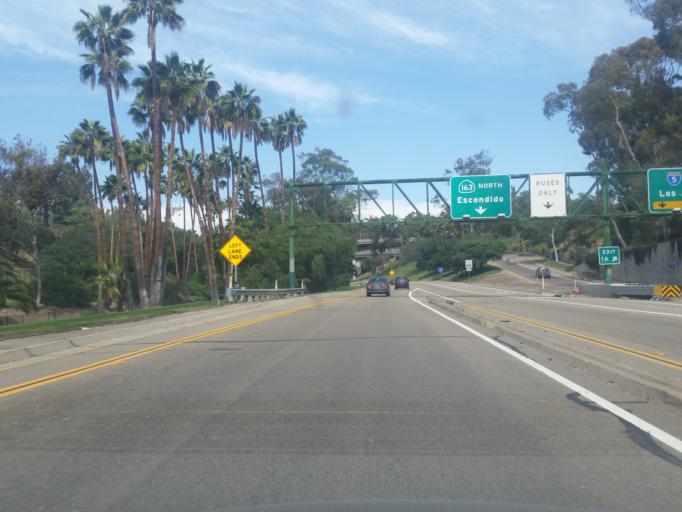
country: US
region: California
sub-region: San Diego County
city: San Diego
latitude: 32.7204
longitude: -117.1548
